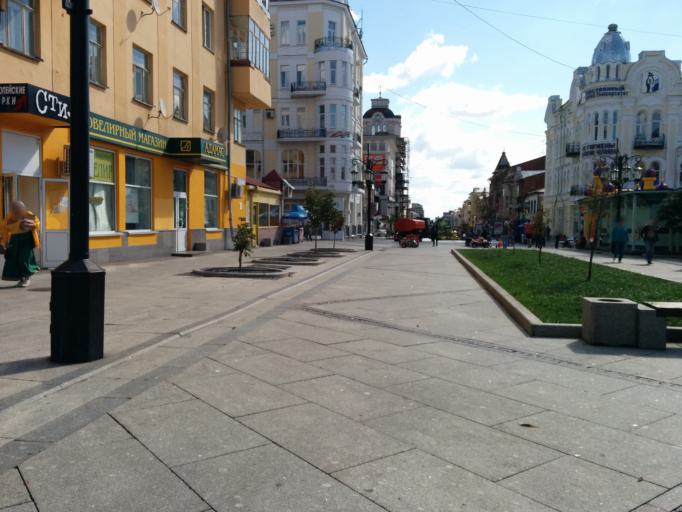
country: RU
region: Samara
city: Samara
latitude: 53.1871
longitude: 50.0930
